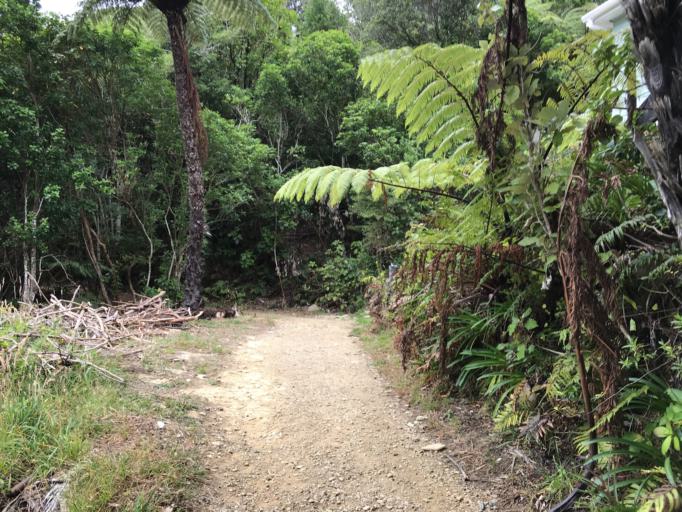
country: NZ
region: Marlborough
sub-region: Marlborough District
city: Picton
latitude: -41.0996
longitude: 174.1857
